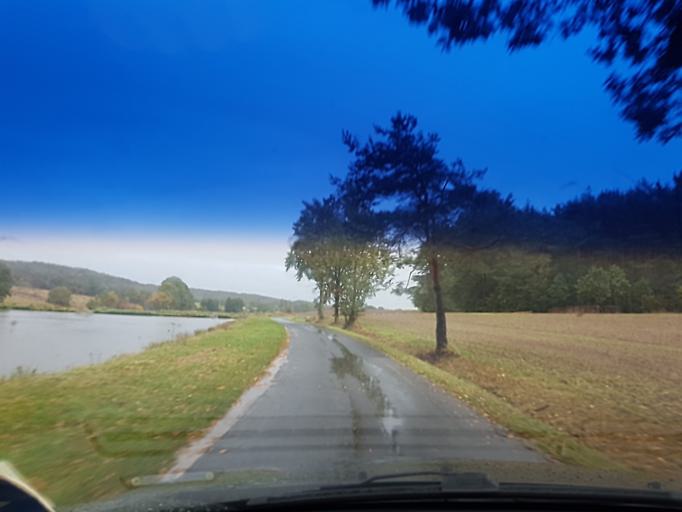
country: DE
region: Bavaria
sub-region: Regierungsbezirk Mittelfranken
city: Wachenroth
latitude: 49.7622
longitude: 10.6774
